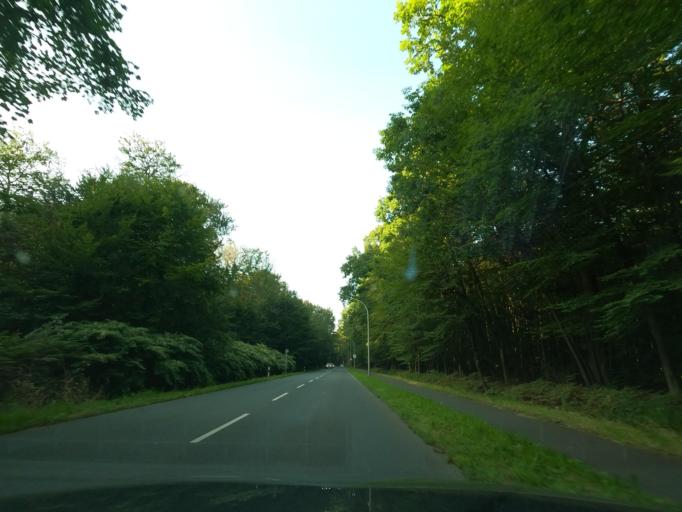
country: DE
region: North Rhine-Westphalia
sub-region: Regierungsbezirk Dusseldorf
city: Dinslaken
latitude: 51.5621
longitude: 6.8295
